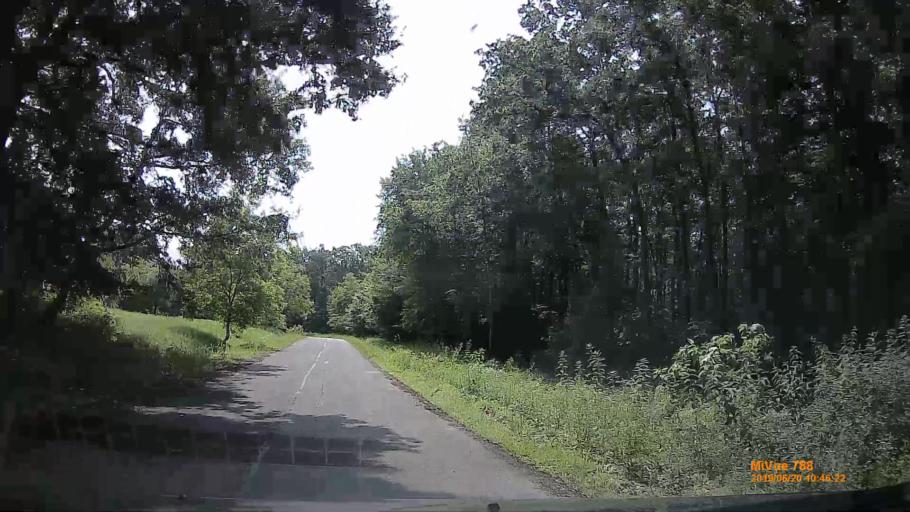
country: HU
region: Baranya
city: Hidas
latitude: 46.1790
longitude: 18.5779
